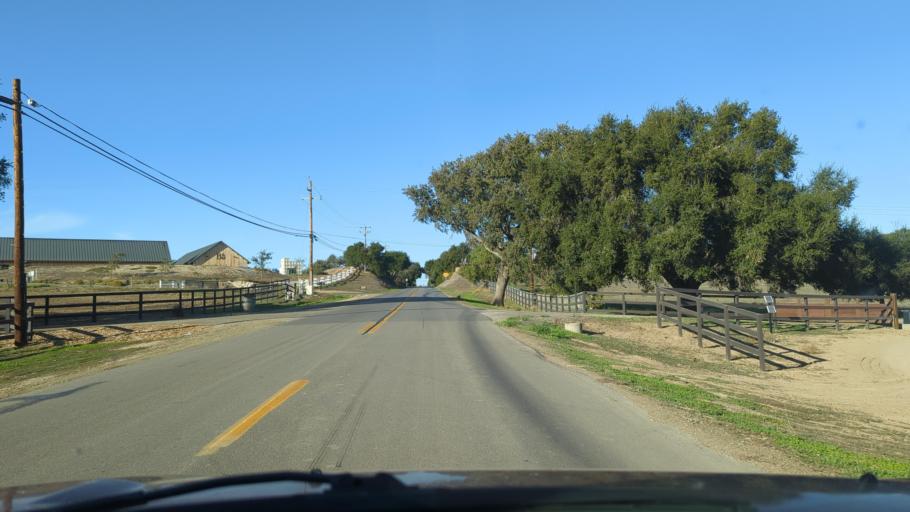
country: US
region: California
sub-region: Santa Barbara County
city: Santa Ynez
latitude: 34.5983
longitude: -120.0983
